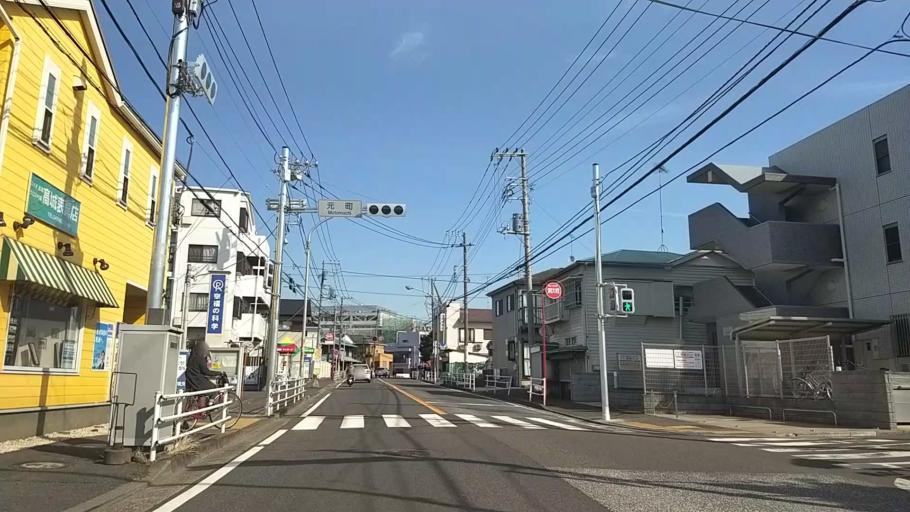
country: JP
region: Kanagawa
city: Fujisawa
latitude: 35.4069
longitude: 139.5381
